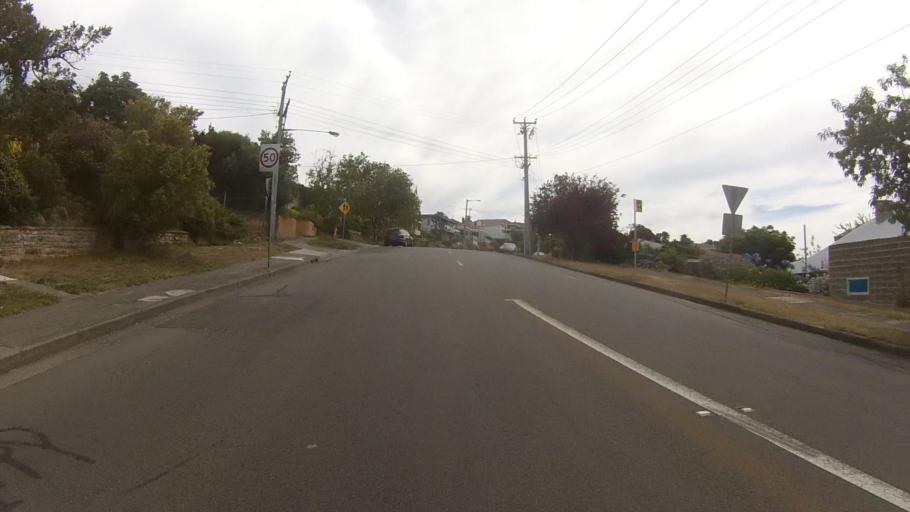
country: AU
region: Tasmania
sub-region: Kingborough
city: Taroona
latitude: -42.9174
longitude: 147.3590
